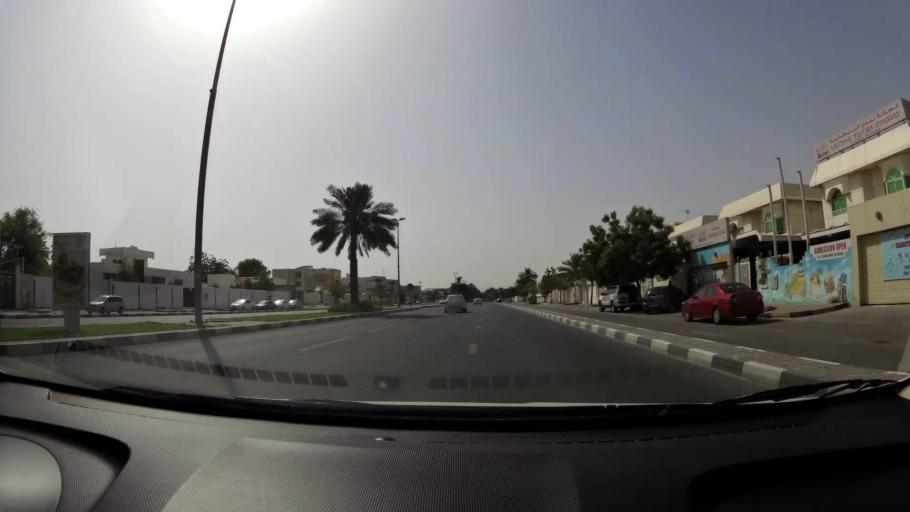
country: AE
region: Ash Shariqah
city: Sharjah
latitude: 25.3517
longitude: 55.4135
